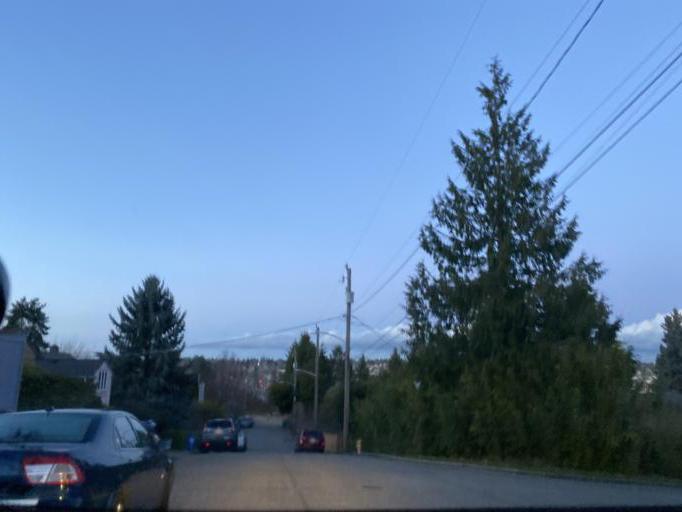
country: US
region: Washington
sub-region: King County
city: Seattle
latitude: 47.6593
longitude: -122.3929
